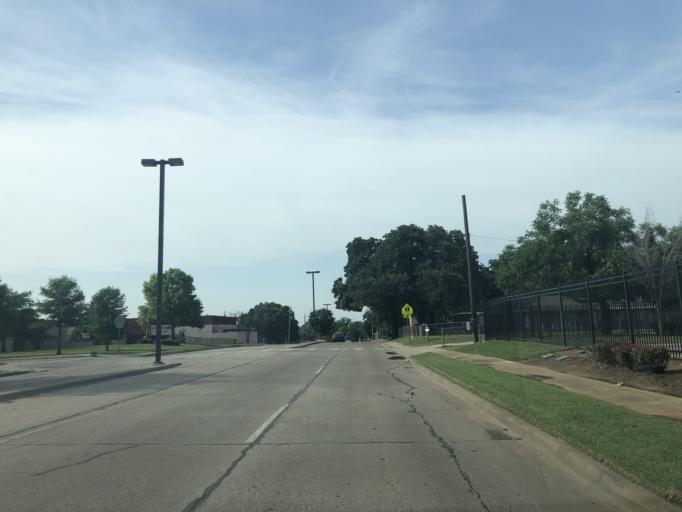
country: US
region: Texas
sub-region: Dallas County
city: Irving
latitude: 32.7980
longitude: -96.9593
